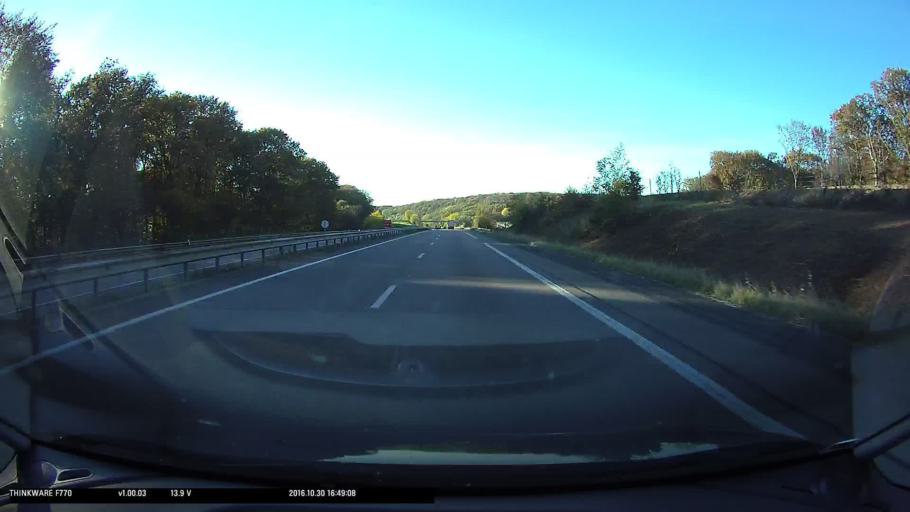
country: FR
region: Franche-Comte
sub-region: Departement du Doubs
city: Pirey
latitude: 47.2760
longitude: 5.9626
